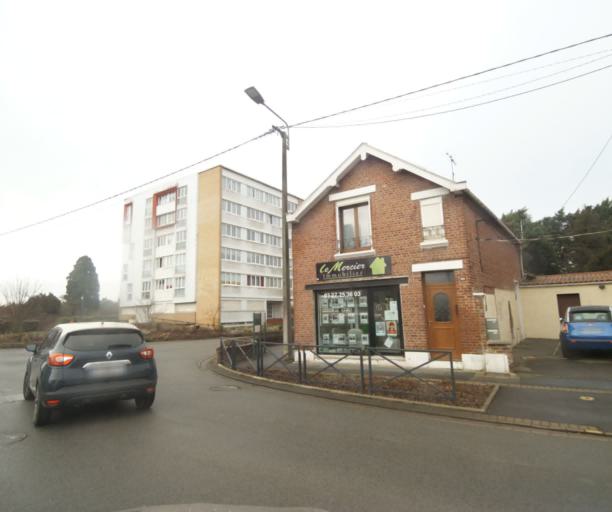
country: FR
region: Nord-Pas-de-Calais
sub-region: Departement du Nord
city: Aulnoy-lez-Valenciennes
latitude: 50.3337
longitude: 3.5237
